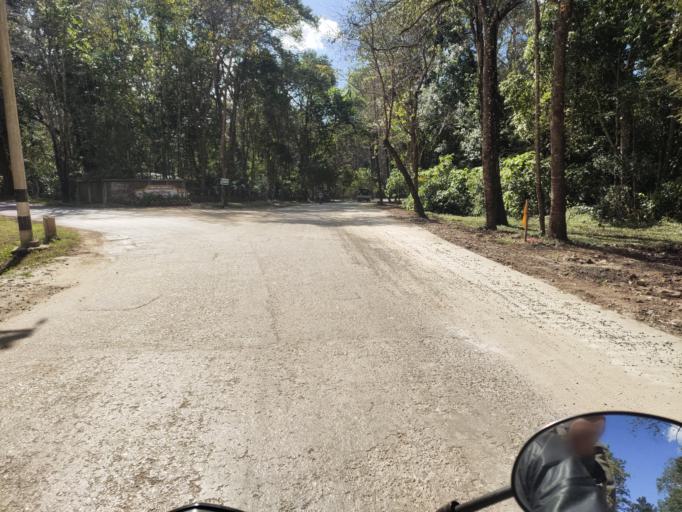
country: MM
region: Mandalay
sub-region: Pyin Oo Lwin District
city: Pyin Oo Lwin
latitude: 21.9880
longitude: 96.4694
